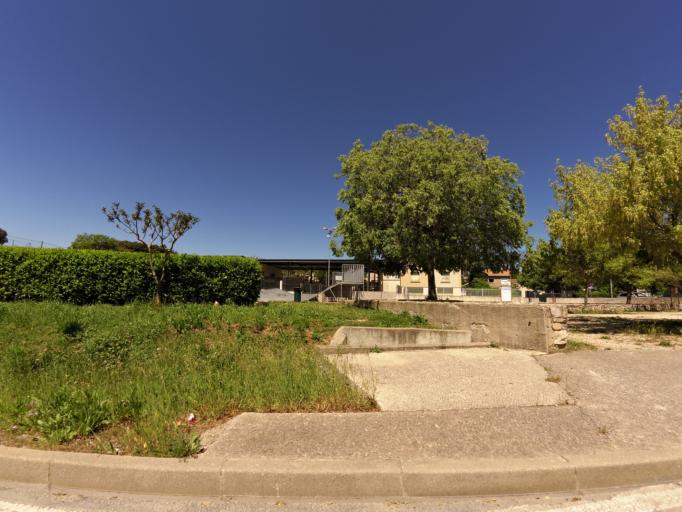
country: FR
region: Languedoc-Roussillon
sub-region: Departement de l'Herault
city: Castries
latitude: 43.6751
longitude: 3.9823
